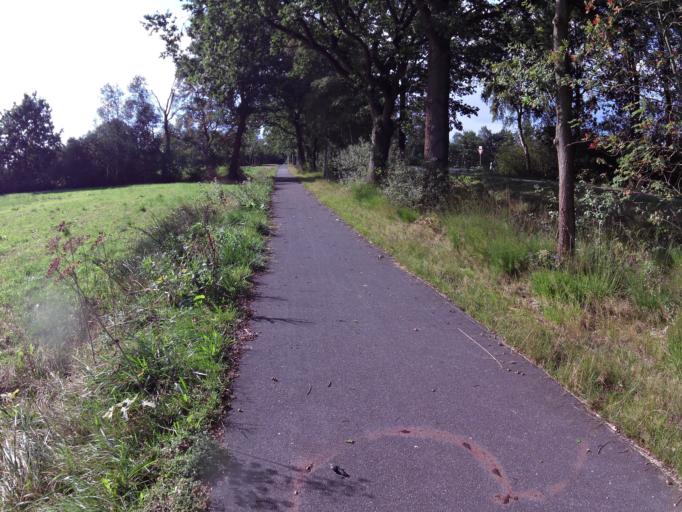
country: DE
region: Lower Saxony
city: Bremervorde
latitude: 53.4657
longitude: 9.1415
